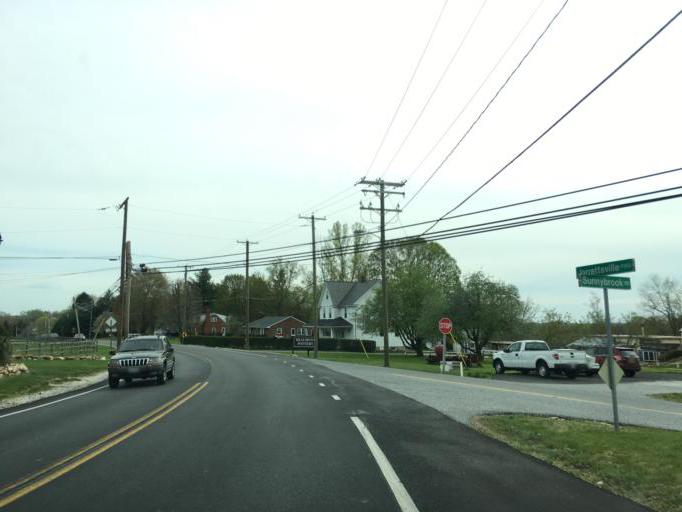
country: US
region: Maryland
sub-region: Baltimore County
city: Hunt Valley
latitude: 39.5035
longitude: -76.5712
